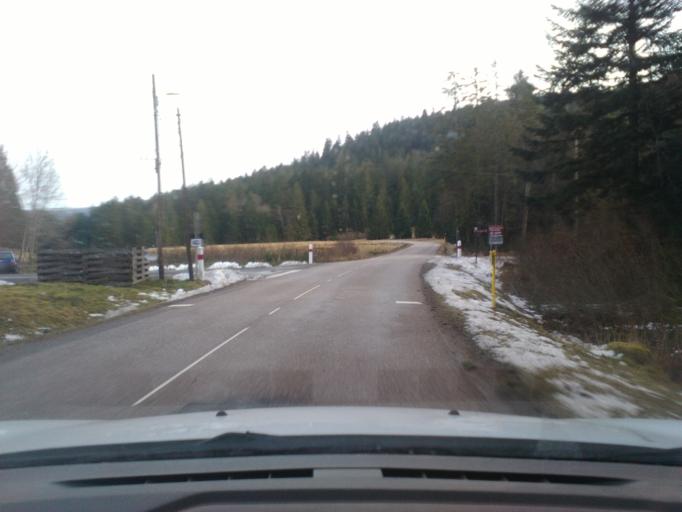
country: FR
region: Lorraine
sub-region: Departement des Vosges
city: Xonrupt-Longemer
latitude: 48.0960
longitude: 6.9552
